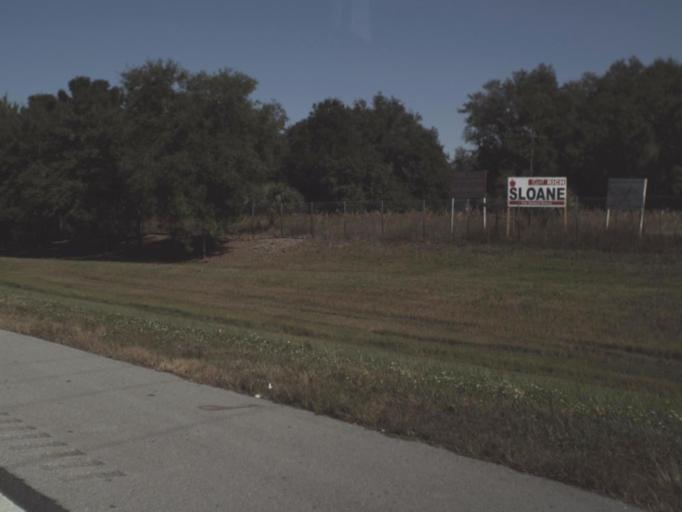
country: US
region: Florida
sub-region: Seminole County
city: Goldenrod
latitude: 28.6336
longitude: -81.2440
